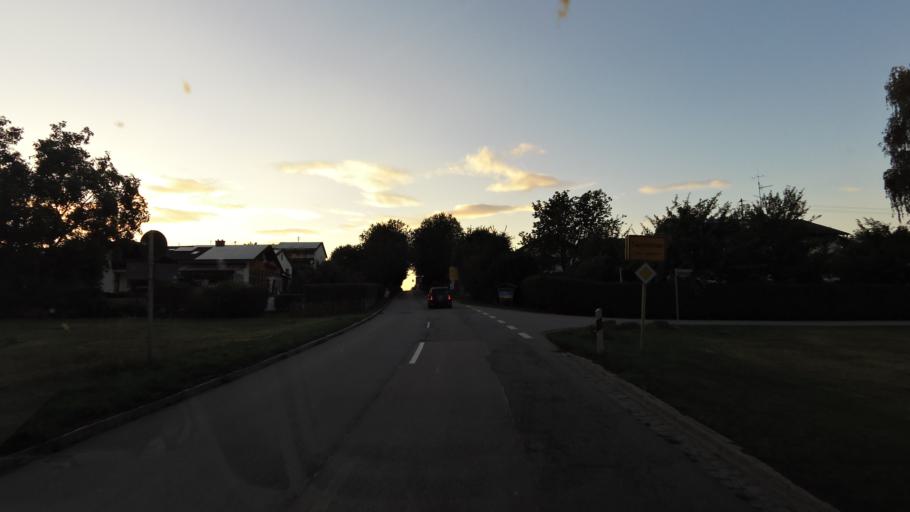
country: DE
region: Bavaria
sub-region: Upper Bavaria
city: Taufkirchen
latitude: 48.1446
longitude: 12.4507
